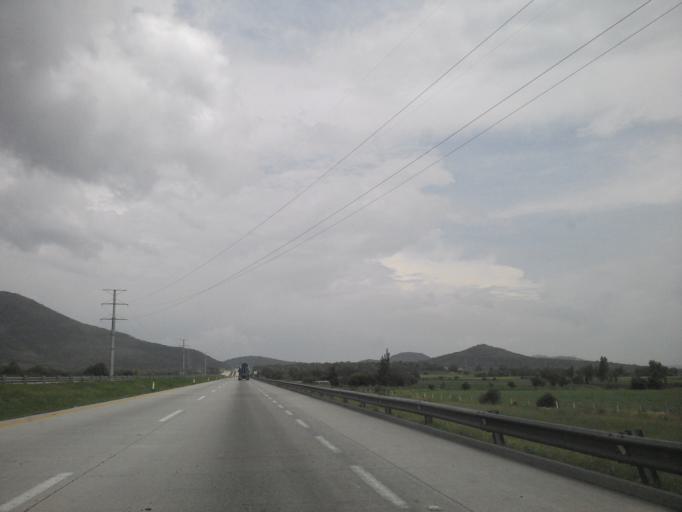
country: MX
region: Hidalgo
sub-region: Atitalaquia
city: Tezoquipa
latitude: 20.0442
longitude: -99.1841
